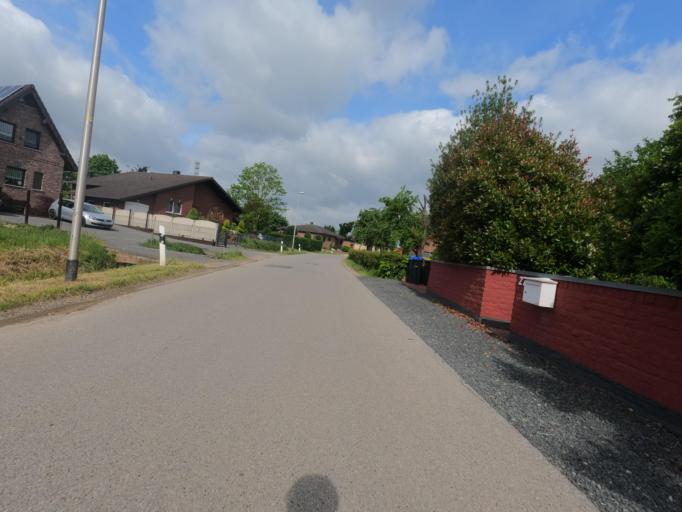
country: DE
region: North Rhine-Westphalia
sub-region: Regierungsbezirk Koln
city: Wassenberg
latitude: 51.0795
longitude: 6.1330
